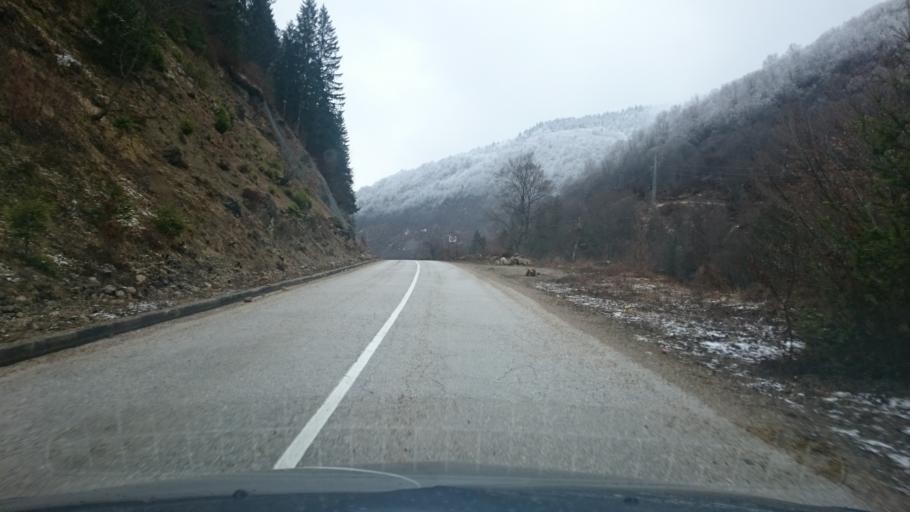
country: BA
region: Republika Srpska
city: Skender Vakuf
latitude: 44.4199
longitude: 17.4184
